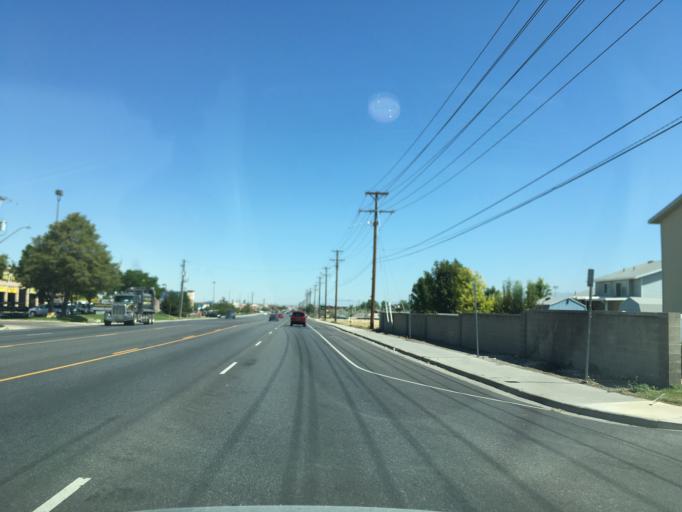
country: US
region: Utah
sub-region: Salt Lake County
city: West Valley City
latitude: 40.6996
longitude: -112.0248
